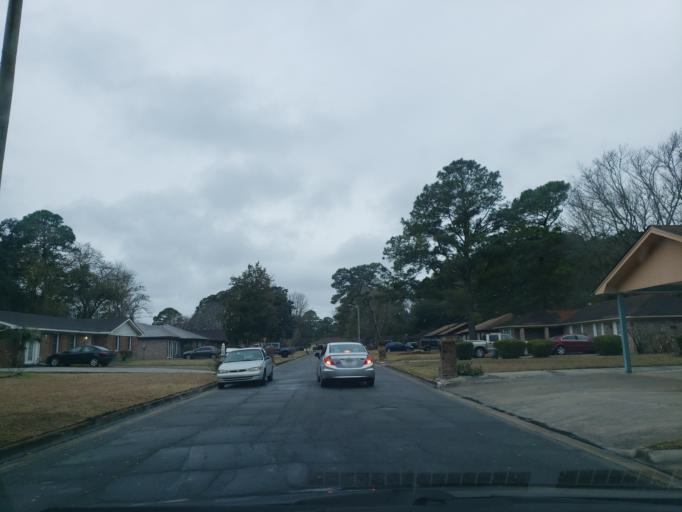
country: US
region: Georgia
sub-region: Chatham County
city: Isle of Hope
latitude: 32.0009
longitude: -81.0679
